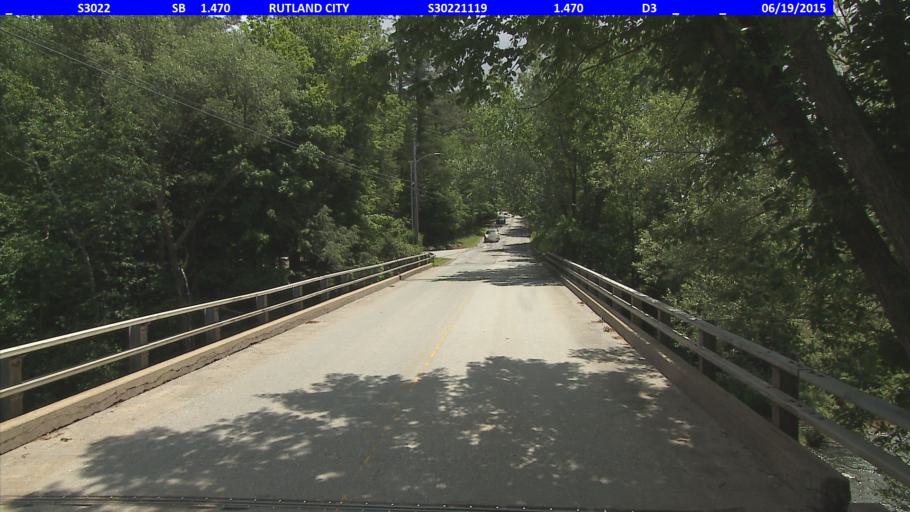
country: US
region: Vermont
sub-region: Rutland County
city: Rutland
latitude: 43.6291
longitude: -72.9882
